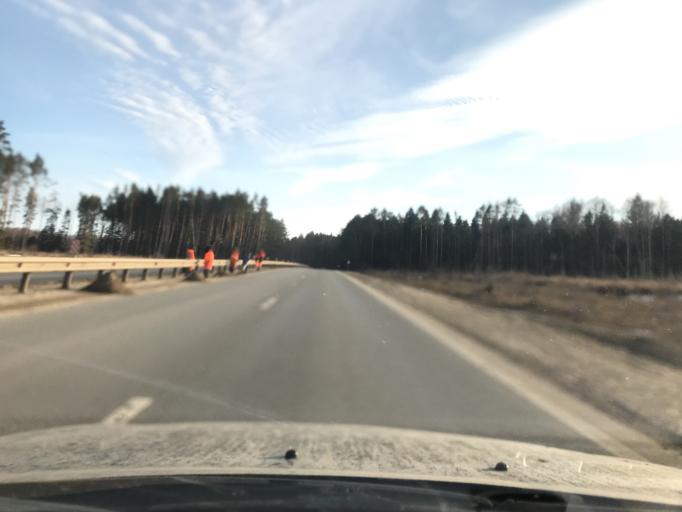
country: RU
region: Kaluga
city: Kaluga
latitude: 54.4171
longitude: 36.2009
